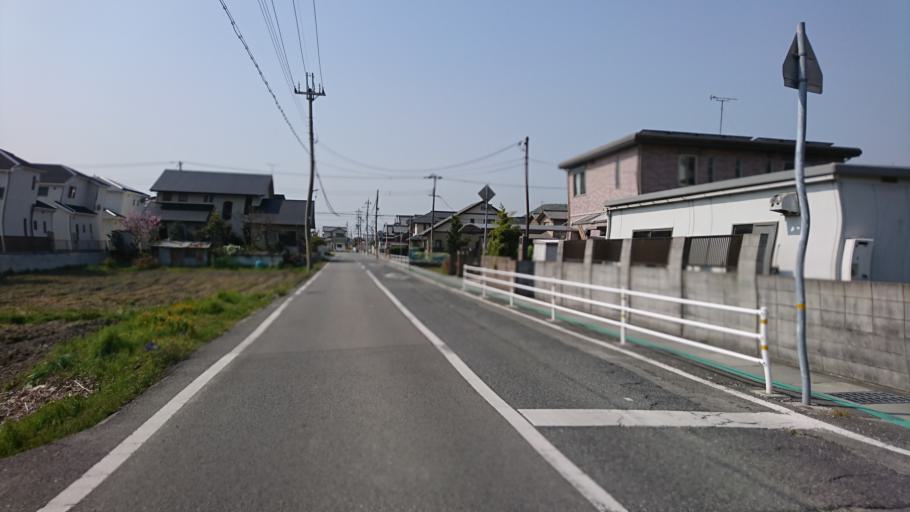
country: JP
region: Hyogo
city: Shirahamacho-usazakiminami
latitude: 34.7887
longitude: 134.7571
